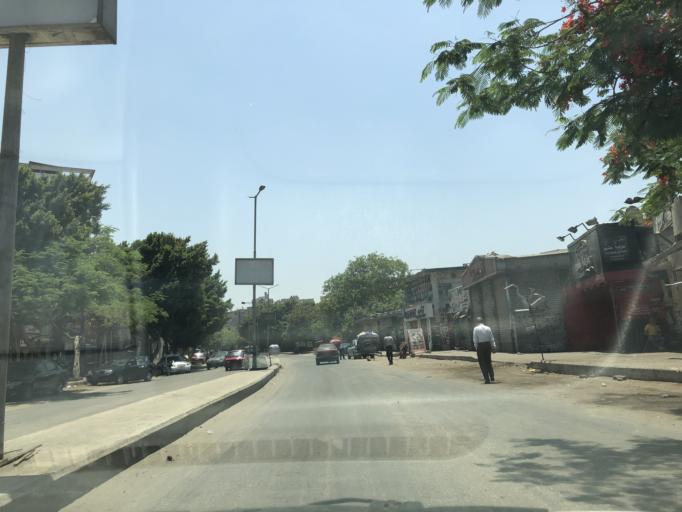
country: EG
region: Muhafazat al Qahirah
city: Cairo
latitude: 30.0673
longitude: 31.2708
